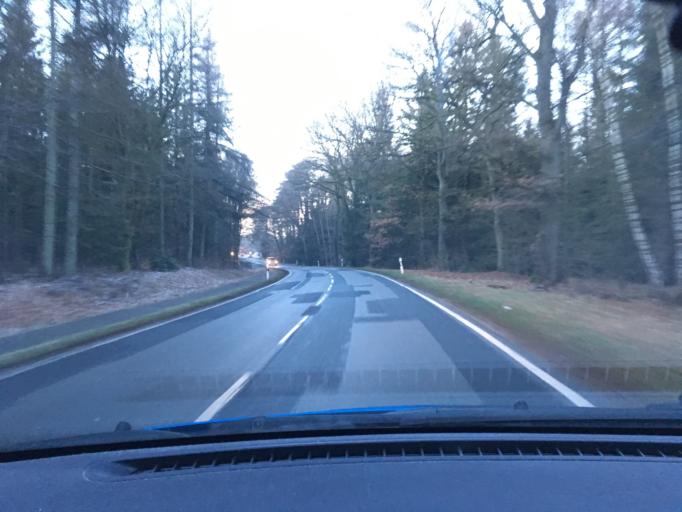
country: DE
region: Lower Saxony
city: Handeloh
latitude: 53.2734
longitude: 9.8789
